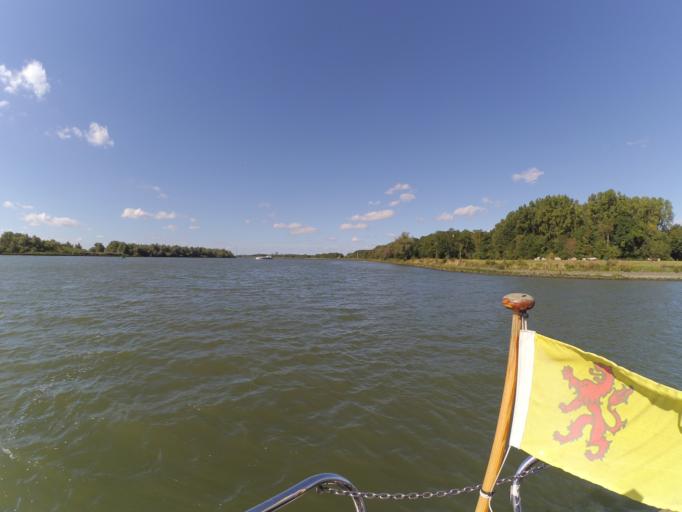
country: NL
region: South Holland
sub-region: Gemeente Albrandswaard
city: Rhoon
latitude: 51.8412
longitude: 4.4228
